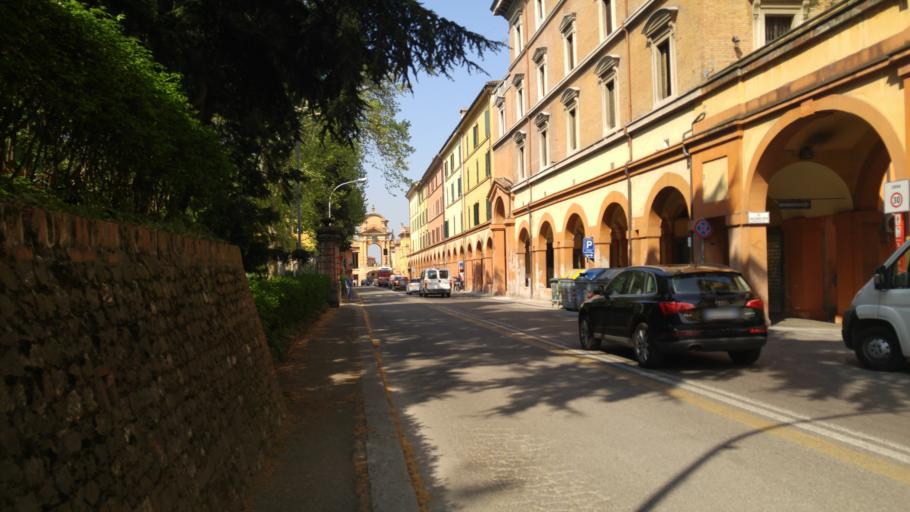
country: IT
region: Emilia-Romagna
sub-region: Provincia di Bologna
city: Bologna
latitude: 44.4900
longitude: 11.3132
